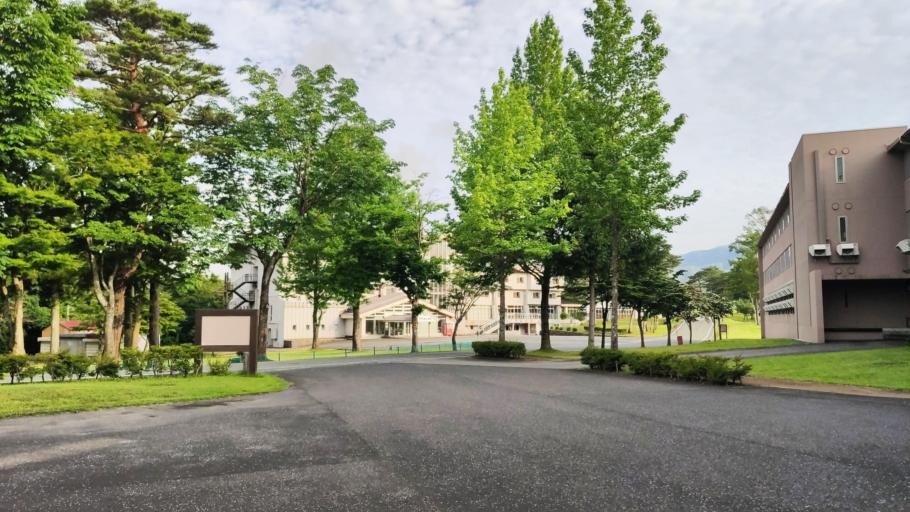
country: JP
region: Tottori
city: Kurayoshi
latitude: 35.2942
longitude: 133.6311
